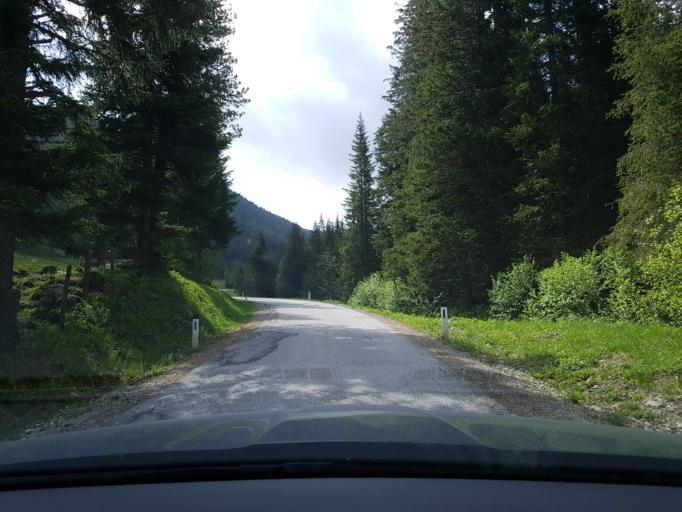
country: AT
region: Salzburg
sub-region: Politischer Bezirk Tamsweg
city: Thomatal
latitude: 47.0287
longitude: 13.7588
